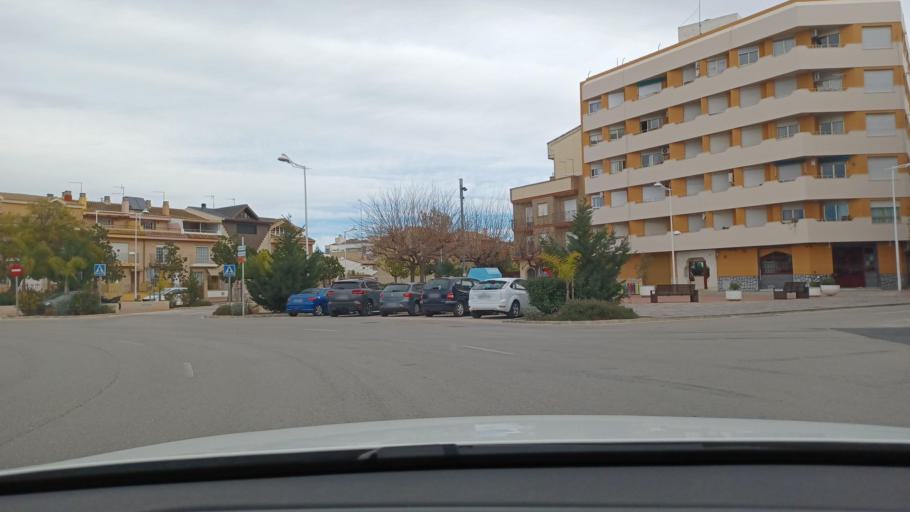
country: ES
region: Valencia
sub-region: Provincia de Valencia
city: Picassent
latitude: 39.3664
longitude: -0.4602
